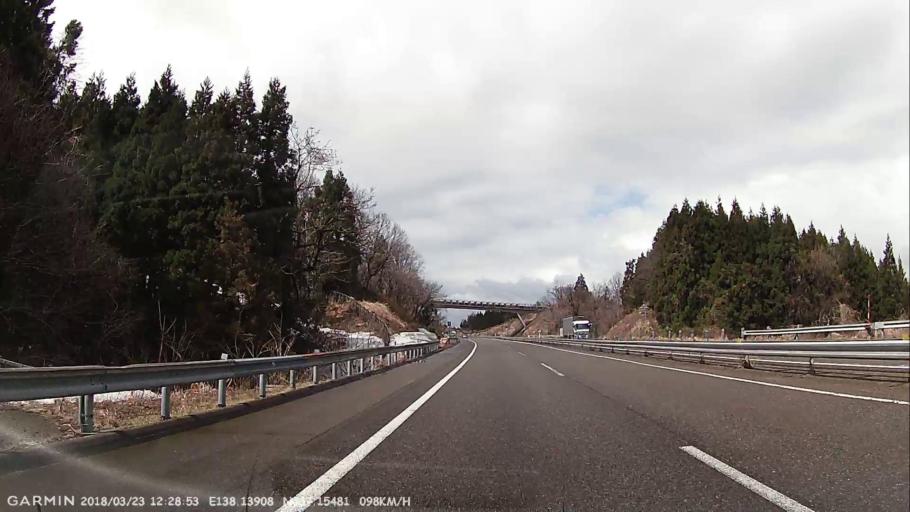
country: JP
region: Niigata
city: Joetsu
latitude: 37.1550
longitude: 138.1389
